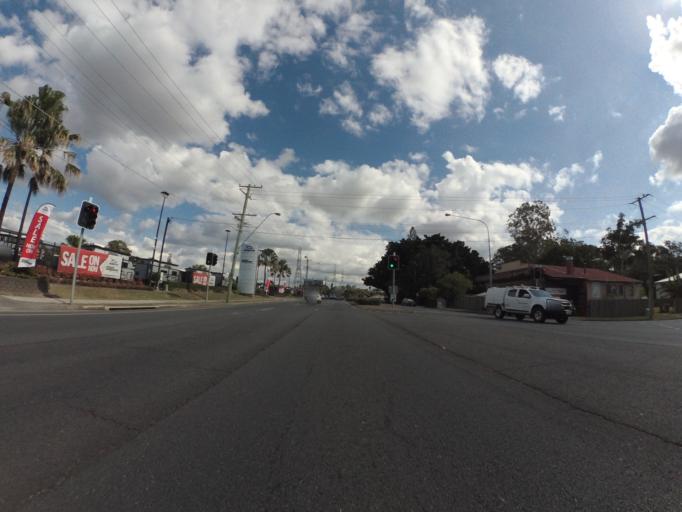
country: AU
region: Queensland
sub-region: Brisbane
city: Belmont
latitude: -27.4745
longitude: 153.1204
